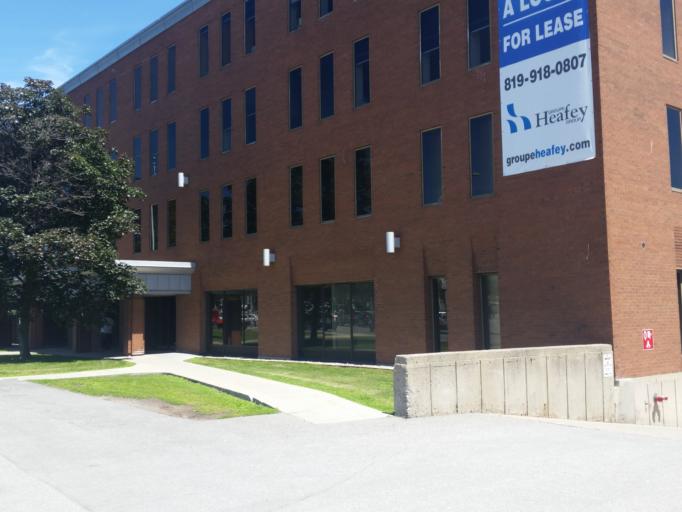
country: CA
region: Quebec
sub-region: Outaouais
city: Gatineau
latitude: 45.4469
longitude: -75.7325
